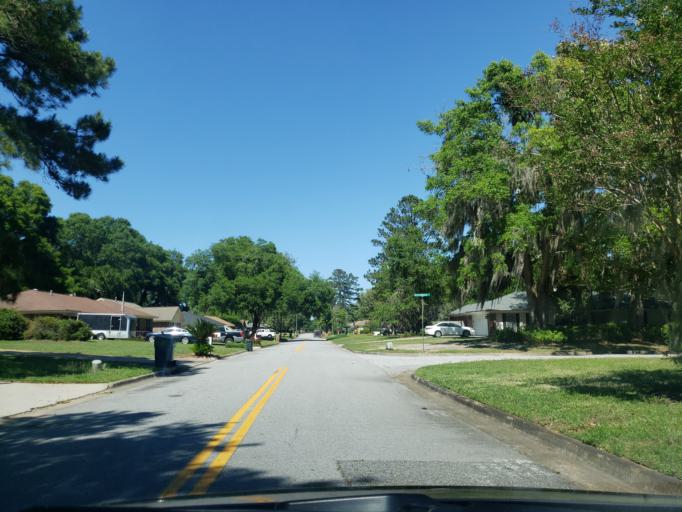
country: US
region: Georgia
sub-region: Chatham County
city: Isle of Hope
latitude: 31.9865
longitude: -81.0945
